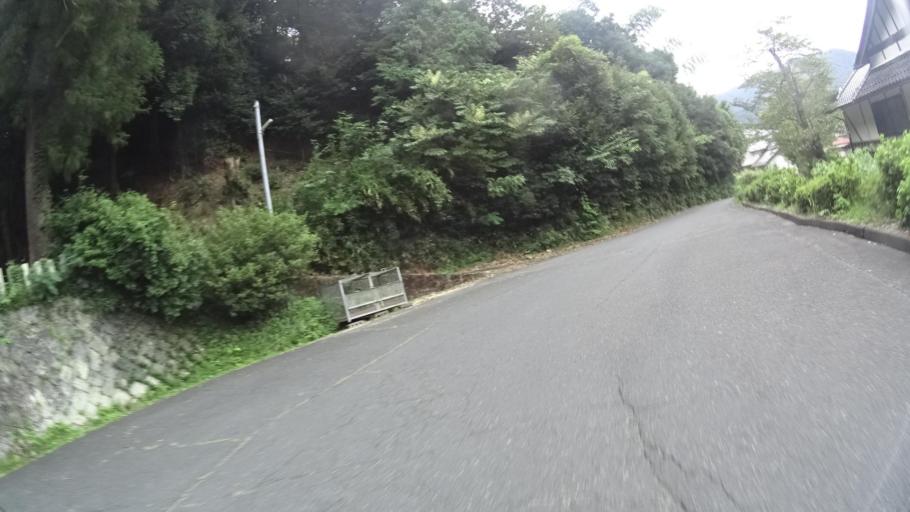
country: JP
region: Kyoto
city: Miyazu
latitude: 35.5280
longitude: 135.1848
